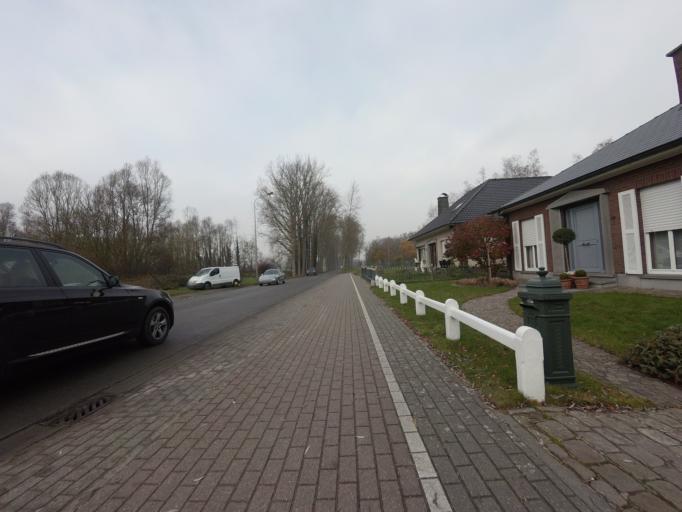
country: BE
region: Flanders
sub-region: Provincie Oost-Vlaanderen
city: Geraardsbergen
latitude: 50.7878
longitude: 3.9065
